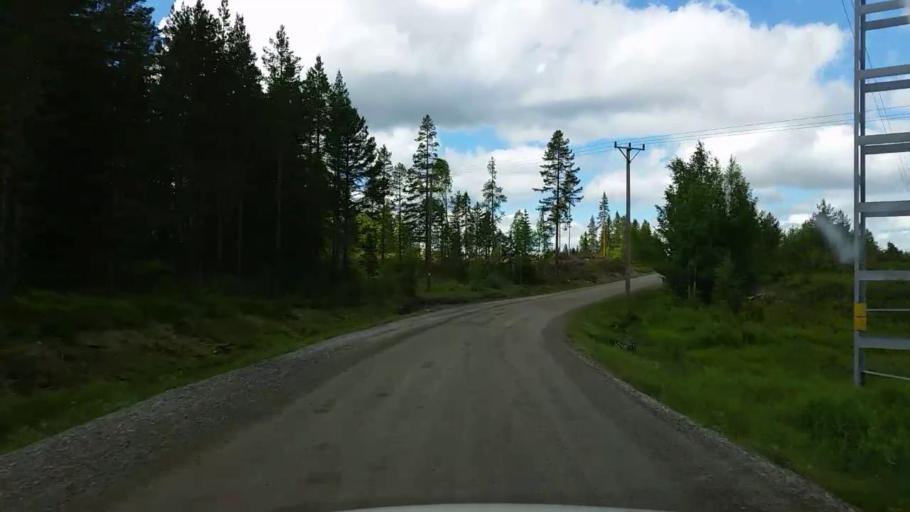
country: SE
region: Gaevleborg
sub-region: Bollnas Kommun
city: Vittsjo
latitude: 61.1771
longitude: 16.1481
